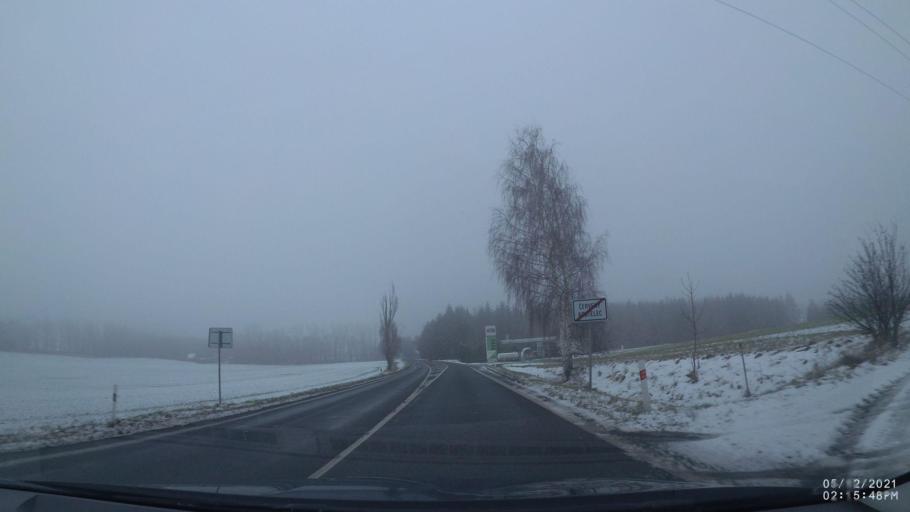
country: CZ
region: Kralovehradecky
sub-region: Okres Nachod
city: Cerveny Kostelec
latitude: 50.4722
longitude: 16.1054
